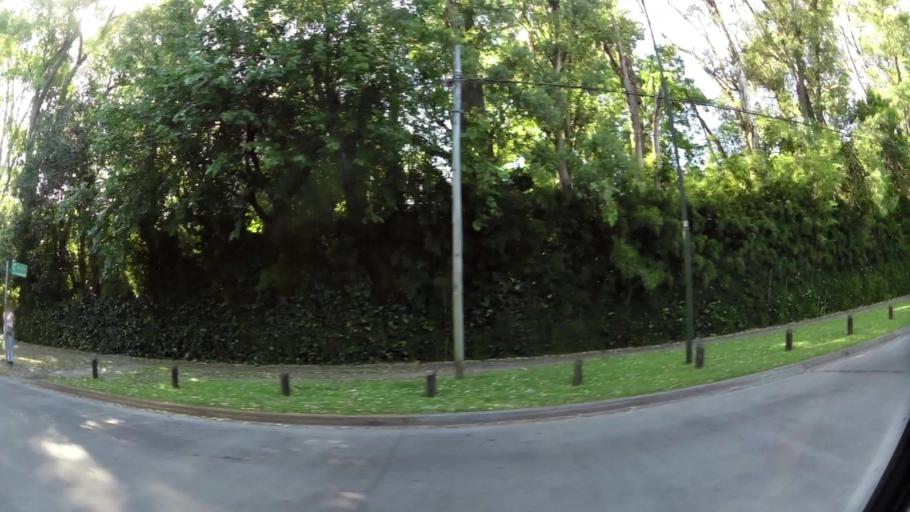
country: AR
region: Buenos Aires
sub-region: Partido de San Isidro
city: San Isidro
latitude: -34.4841
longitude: -58.5424
